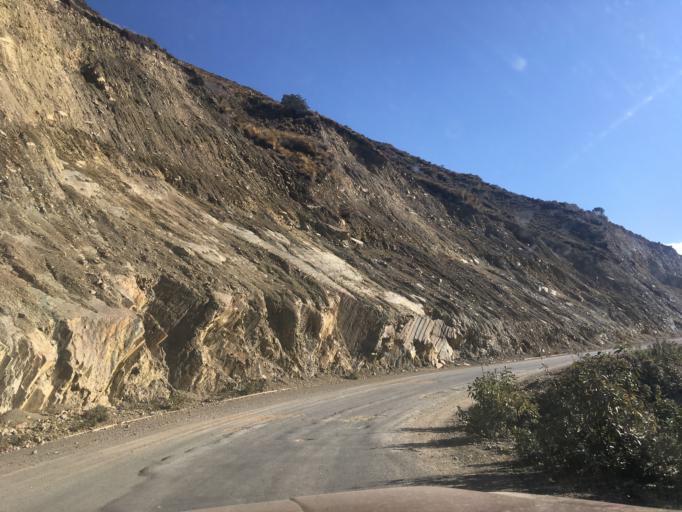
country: BO
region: La Paz
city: Quime
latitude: -17.0151
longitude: -67.2779
